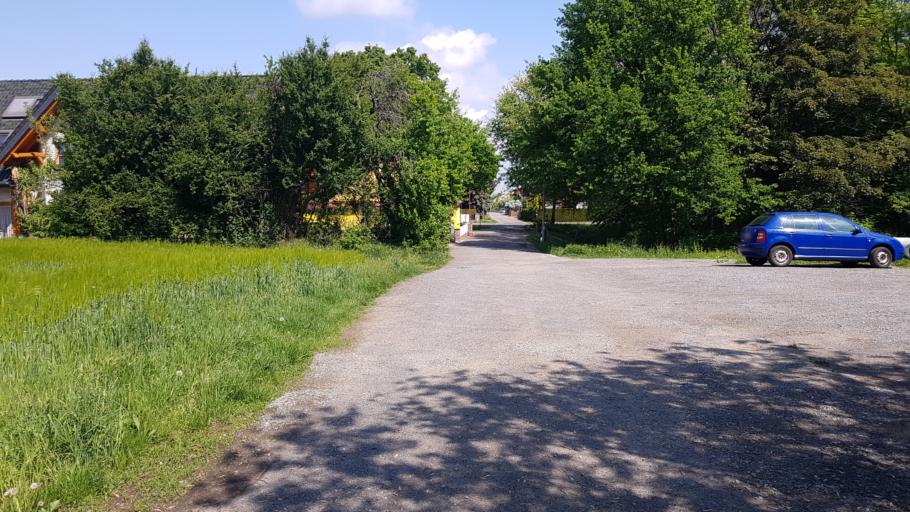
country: DE
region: Brandenburg
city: Doberlug-Kirchhain
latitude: 51.6333
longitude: 13.5526
